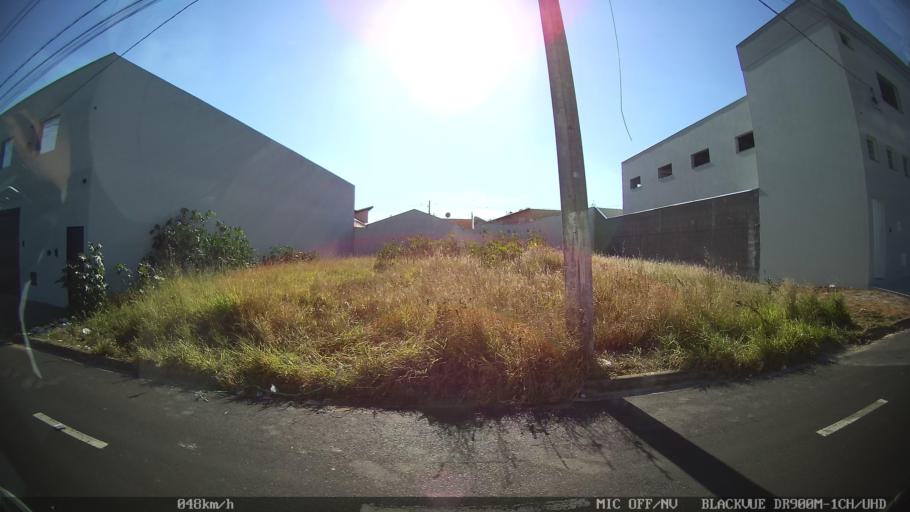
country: BR
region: Sao Paulo
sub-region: Franca
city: Franca
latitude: -20.5126
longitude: -47.4256
